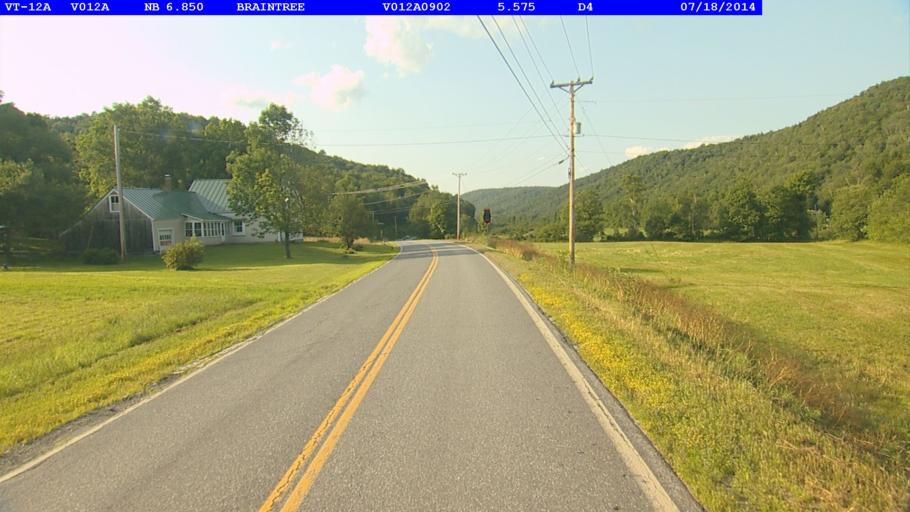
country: US
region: Vermont
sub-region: Orange County
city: Randolph
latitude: 43.9876
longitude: -72.7525
